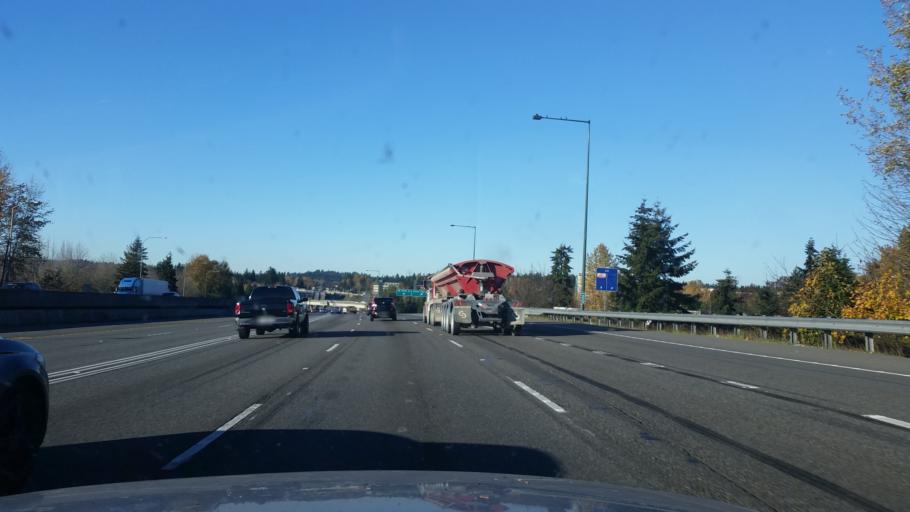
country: US
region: Washington
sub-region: King County
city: Kingsgate
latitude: 47.7054
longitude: -122.1797
